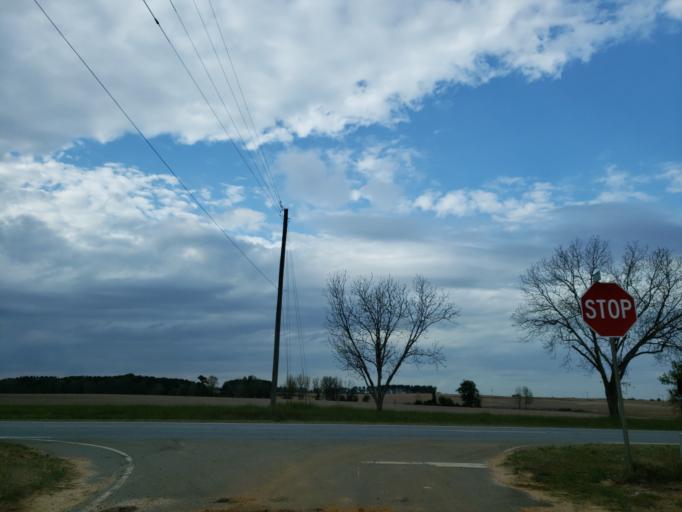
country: US
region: Georgia
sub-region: Dooly County
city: Vienna
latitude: 32.1308
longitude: -83.7040
